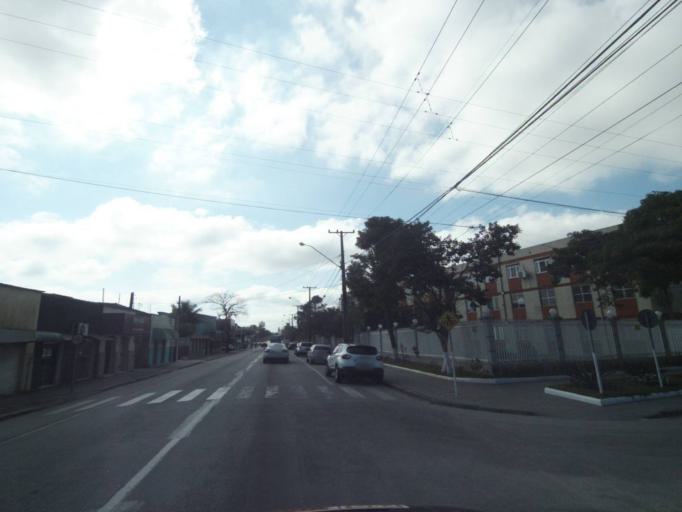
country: BR
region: Parana
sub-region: Paranagua
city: Paranagua
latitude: -25.5269
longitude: -48.5163
